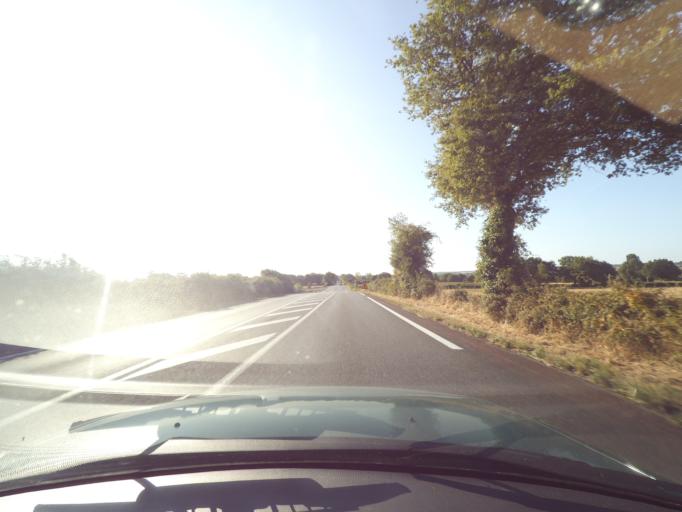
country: FR
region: Poitou-Charentes
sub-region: Departement des Deux-Sevres
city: Chiche
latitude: 46.8056
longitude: -0.3774
